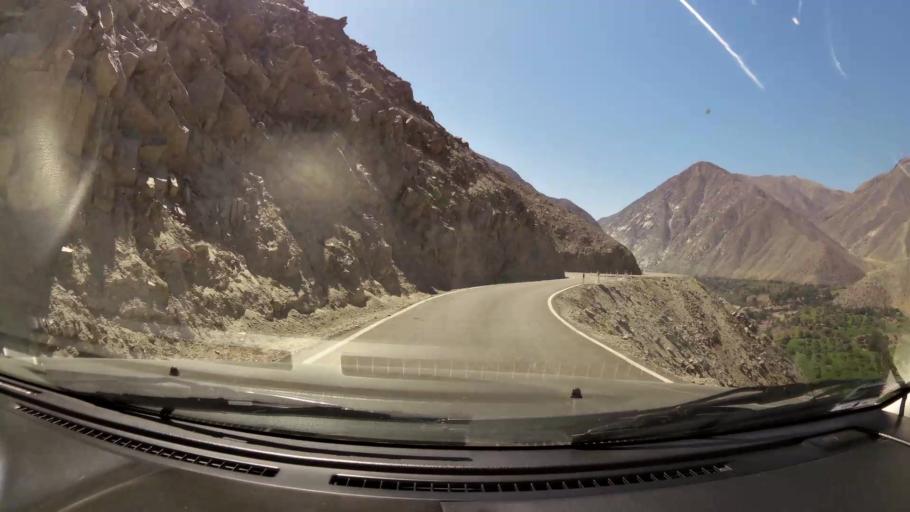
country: PE
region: Ica
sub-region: Provincia de Pisco
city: Huancano
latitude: -13.8373
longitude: -75.5548
